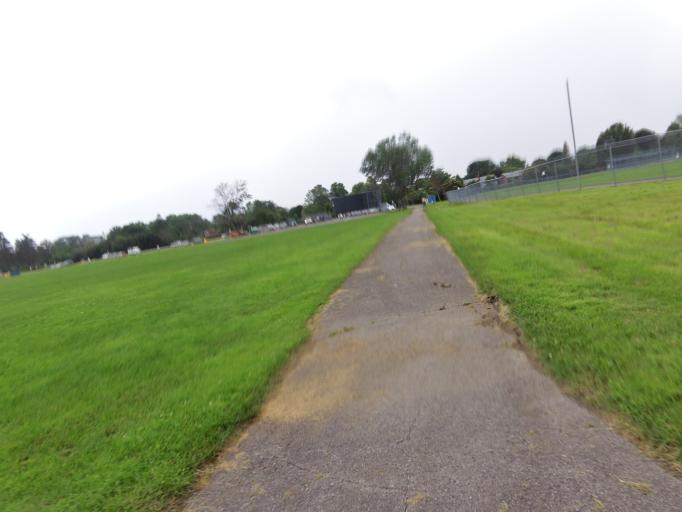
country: CA
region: Ontario
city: Bells Corners
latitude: 45.3493
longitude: -75.7730
